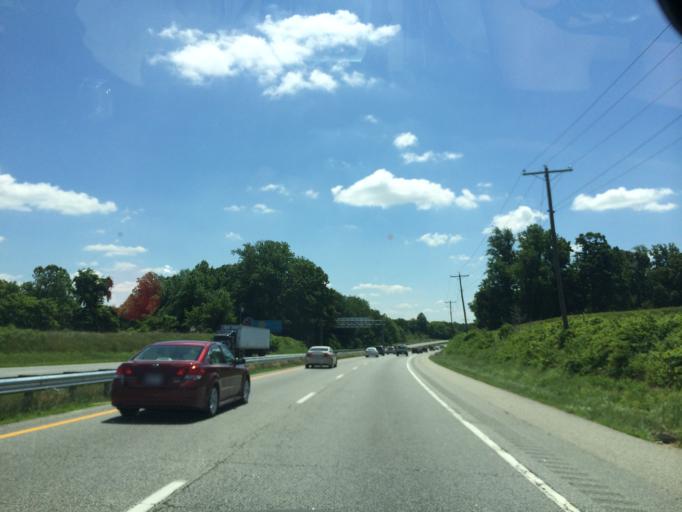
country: US
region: Maryland
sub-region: Queen Anne's County
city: Centreville
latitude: 38.9518
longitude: -76.0701
